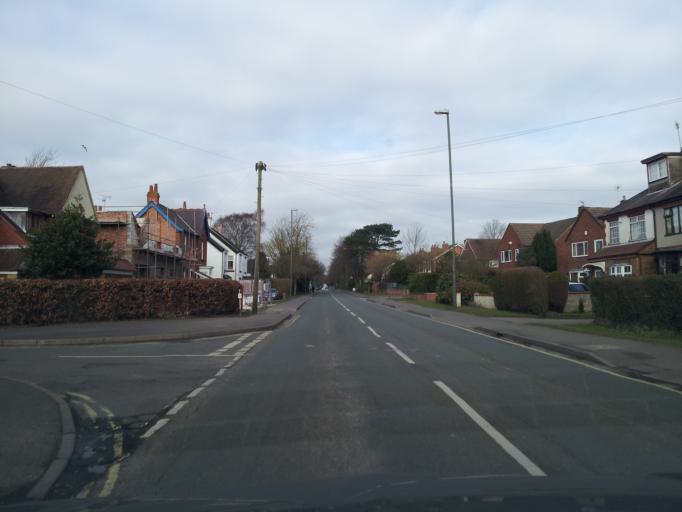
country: GB
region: England
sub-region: Derbyshire
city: Findern
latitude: 52.9099
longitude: -1.5438
